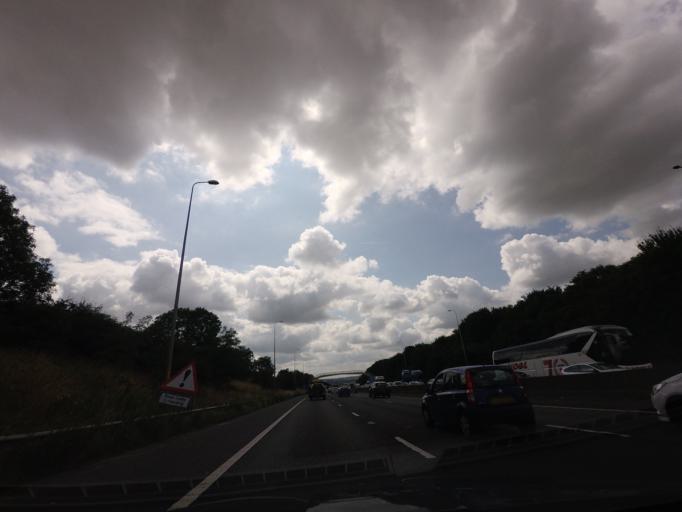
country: GB
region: England
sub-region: Borough of Wigan
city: Shevington
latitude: 53.5843
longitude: -2.6935
